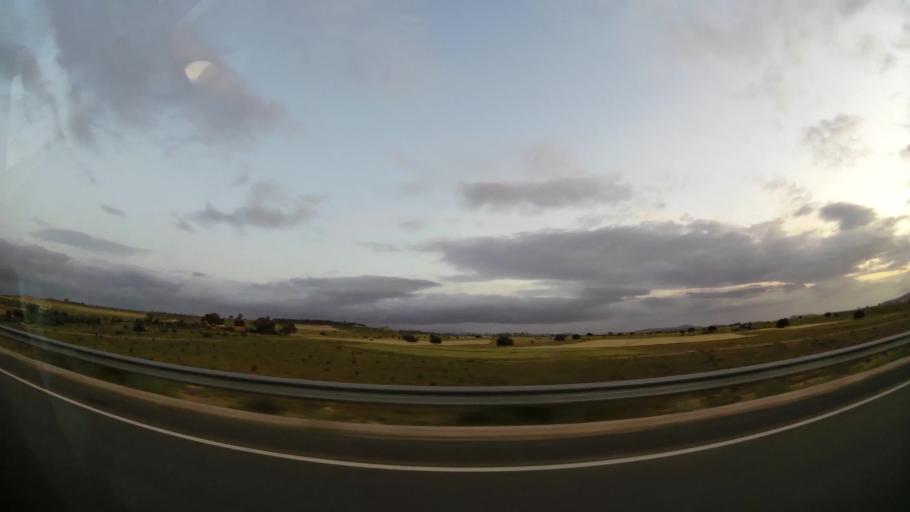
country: MA
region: Oriental
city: El Aioun
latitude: 34.6235
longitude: -2.4999
